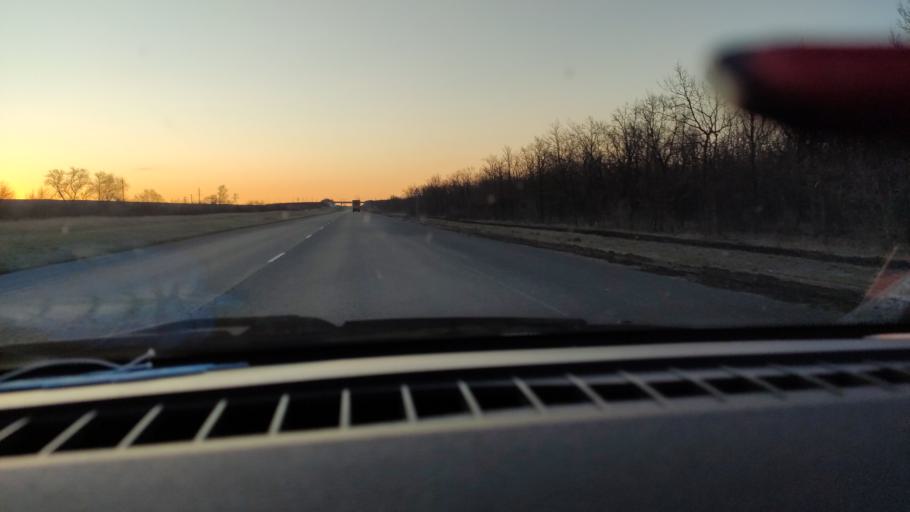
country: RU
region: Saratov
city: Yelshanka
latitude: 51.8267
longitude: 46.2781
